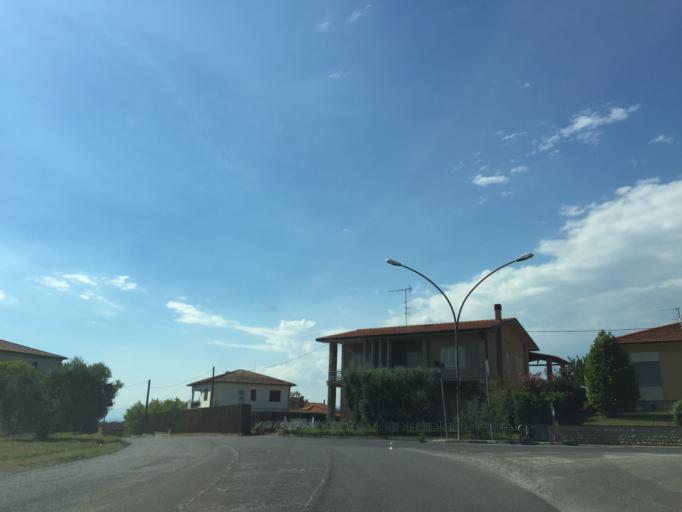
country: IT
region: Tuscany
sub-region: Provincia di Pistoia
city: San Rocco
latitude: 43.8241
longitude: 10.8696
